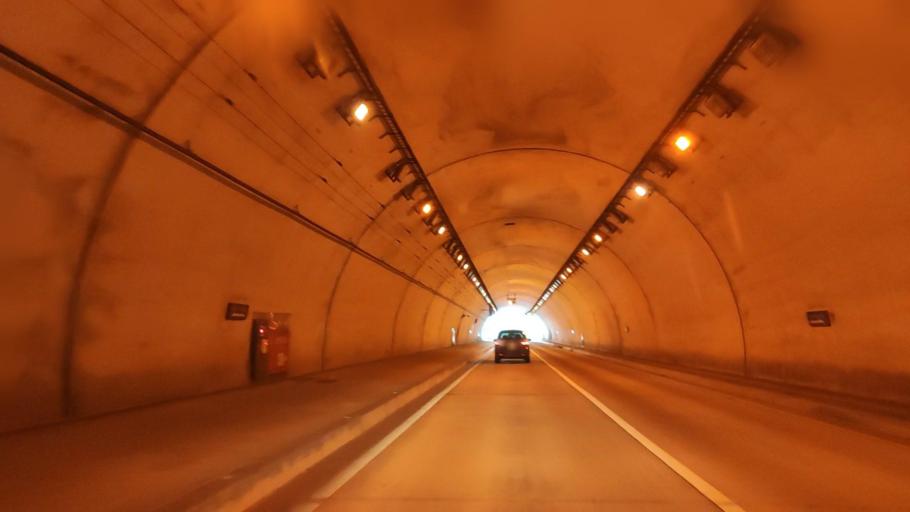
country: JP
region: Ehime
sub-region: Shikoku-chuo Shi
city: Matsuyama
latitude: 33.8864
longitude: 132.7075
